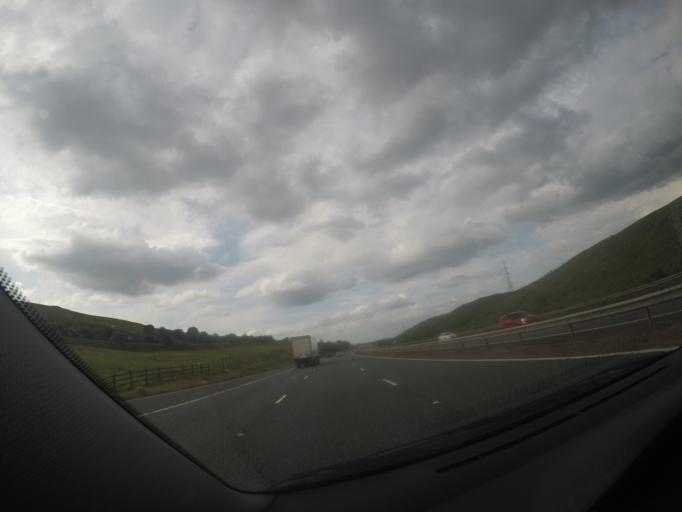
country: GB
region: Scotland
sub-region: South Lanarkshire
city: Douglas
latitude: 55.5501
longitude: -3.8003
